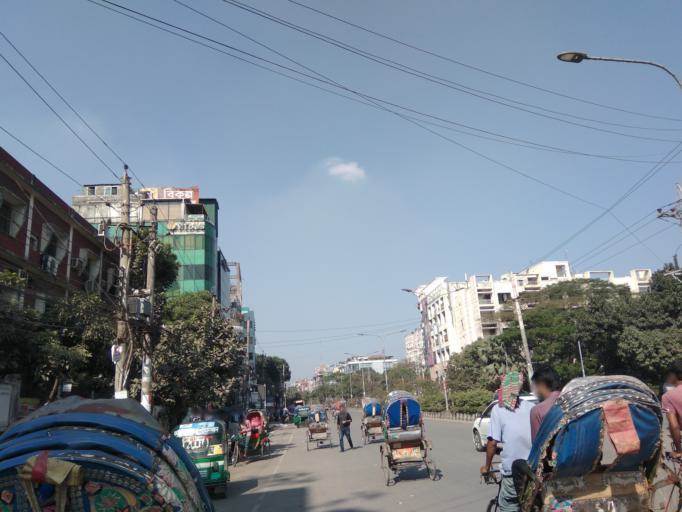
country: BD
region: Dhaka
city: Azimpur
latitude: 23.7412
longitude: 90.3745
